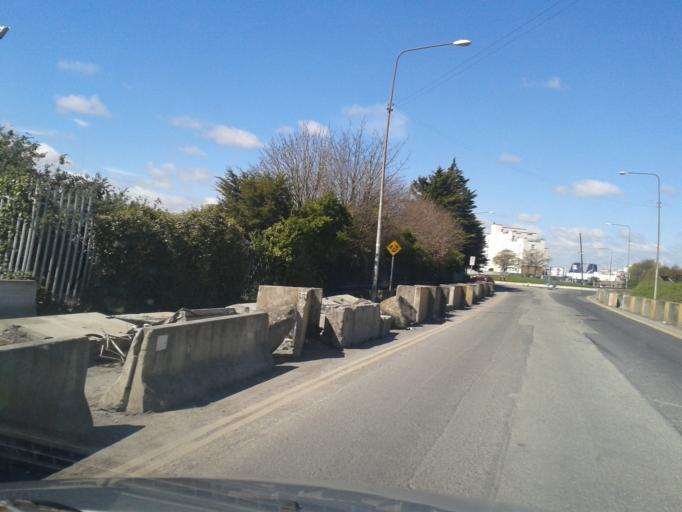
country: IE
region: Leinster
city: Sandymount
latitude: 53.3402
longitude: -6.2115
